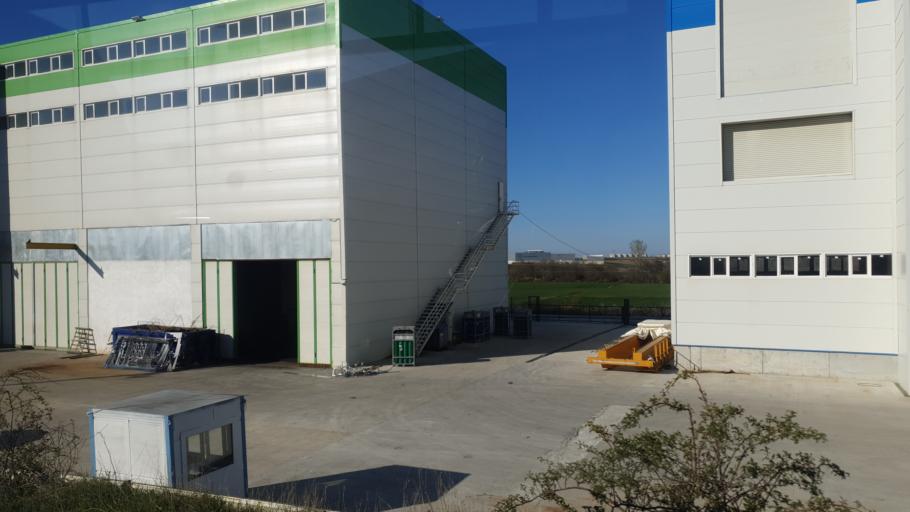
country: TR
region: Tekirdag
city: Velimese
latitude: 41.2566
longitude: 27.9095
